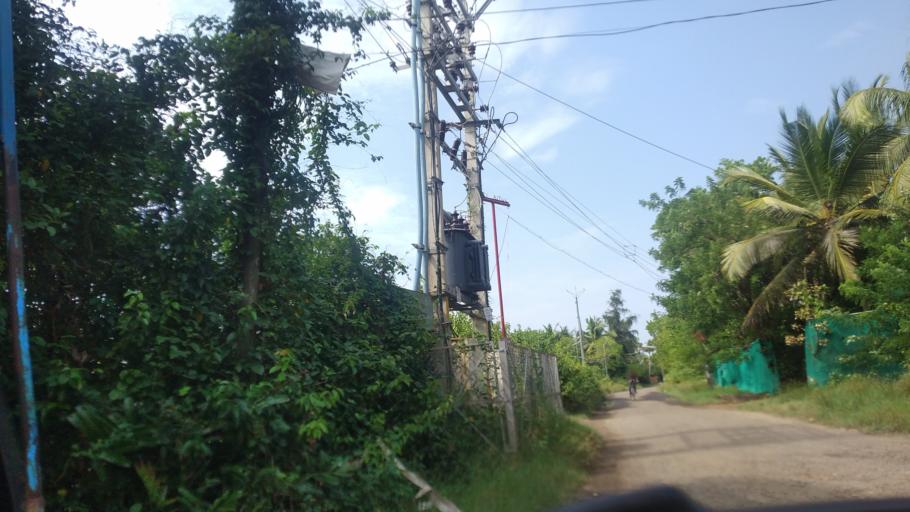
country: IN
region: Kerala
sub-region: Ernakulam
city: Elur
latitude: 10.0524
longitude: 76.2034
